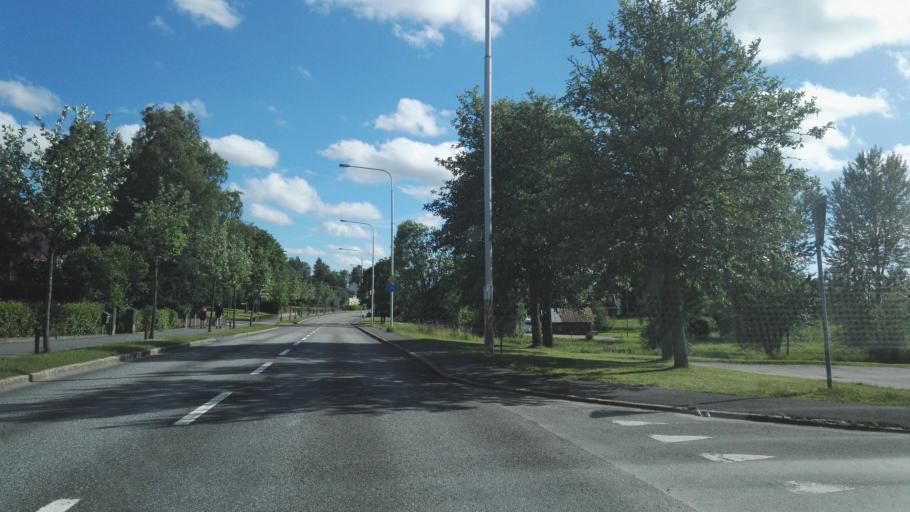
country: SE
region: Joenkoeping
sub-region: Savsjo Kommun
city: Vrigstad
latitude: 57.3540
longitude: 14.4756
